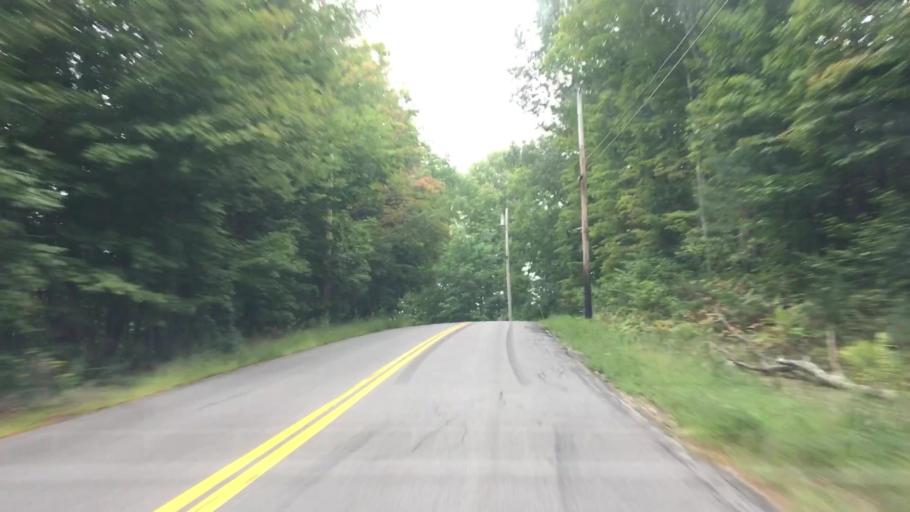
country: US
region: Maine
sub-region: Cumberland County
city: New Gloucester
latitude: 43.9061
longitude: -70.2177
